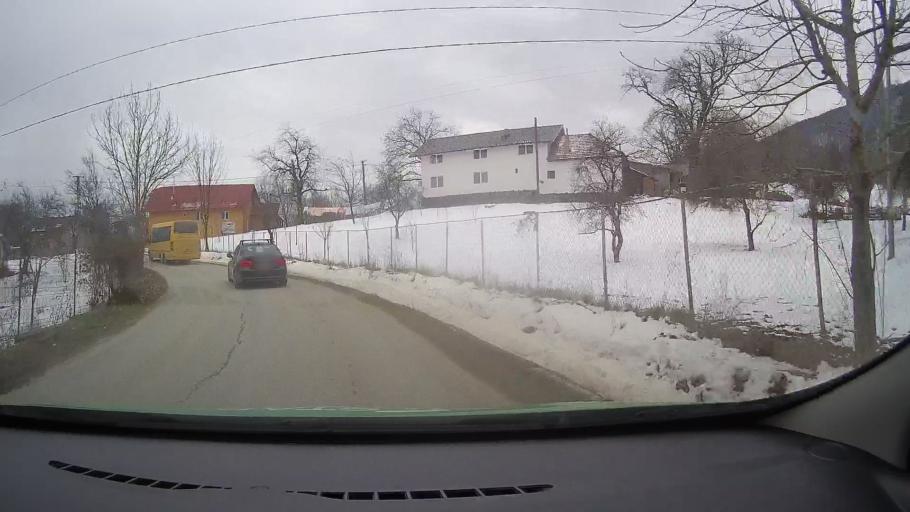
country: RO
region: Brasov
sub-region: Comuna Bran
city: Bran
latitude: 45.5328
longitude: 25.3416
